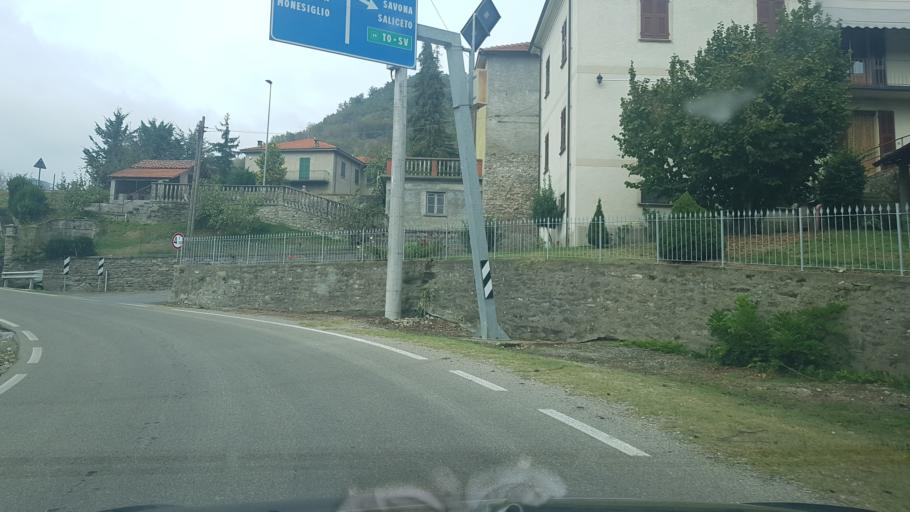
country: IT
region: Piedmont
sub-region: Provincia di Cuneo
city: Camerana
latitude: 44.4372
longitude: 8.1531
